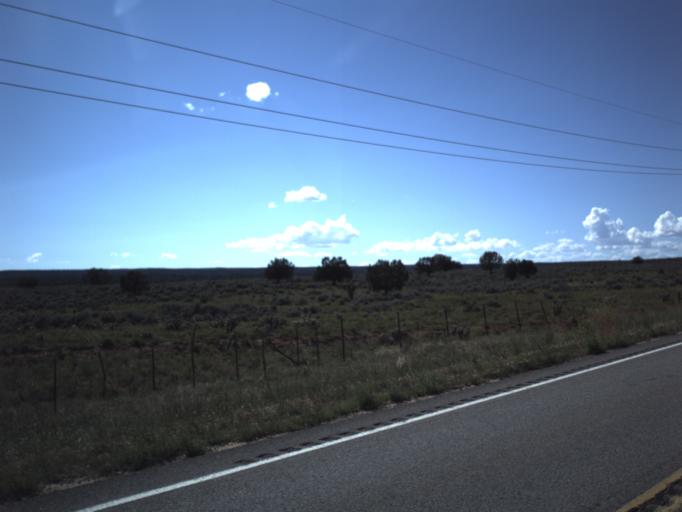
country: US
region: Arizona
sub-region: Mohave County
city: Colorado City
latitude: 37.0485
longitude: -113.0894
